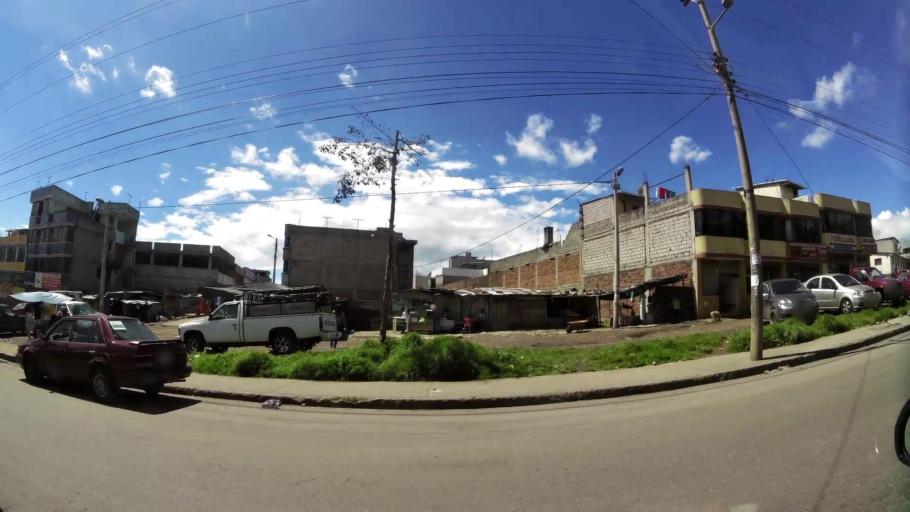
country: EC
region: Pichincha
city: Quito
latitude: -0.3195
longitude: -78.5638
